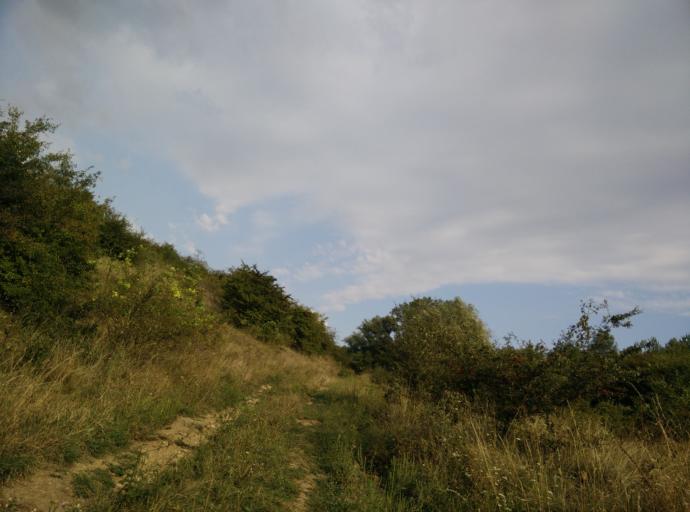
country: HU
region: Pest
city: Paty
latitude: 47.5026
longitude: 18.8449
